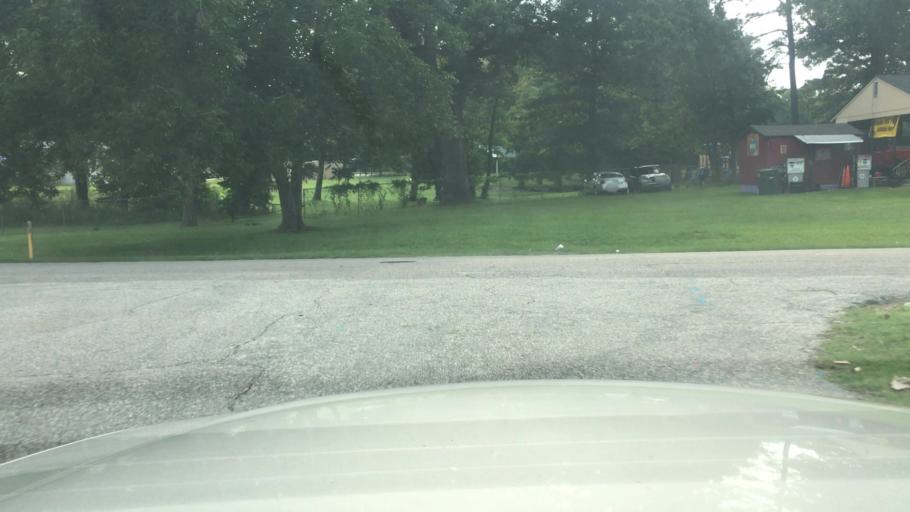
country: US
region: North Carolina
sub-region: Cumberland County
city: Fayetteville
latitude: 35.0953
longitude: -78.9425
